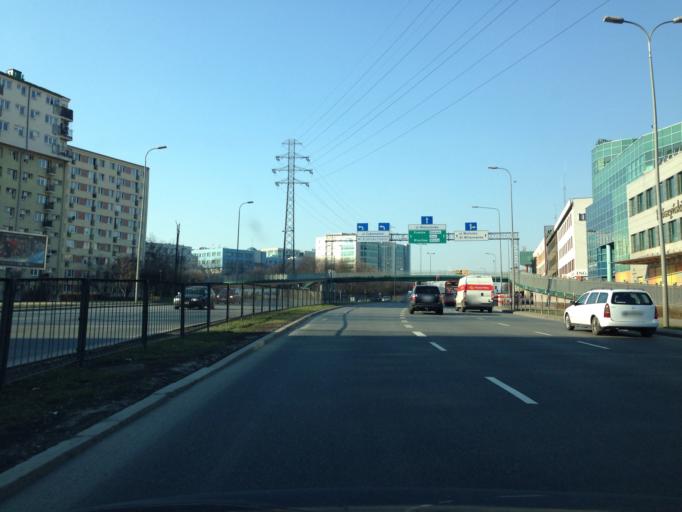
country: PL
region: Masovian Voivodeship
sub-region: Warszawa
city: Mokotow
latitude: 52.1735
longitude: 21.0031
